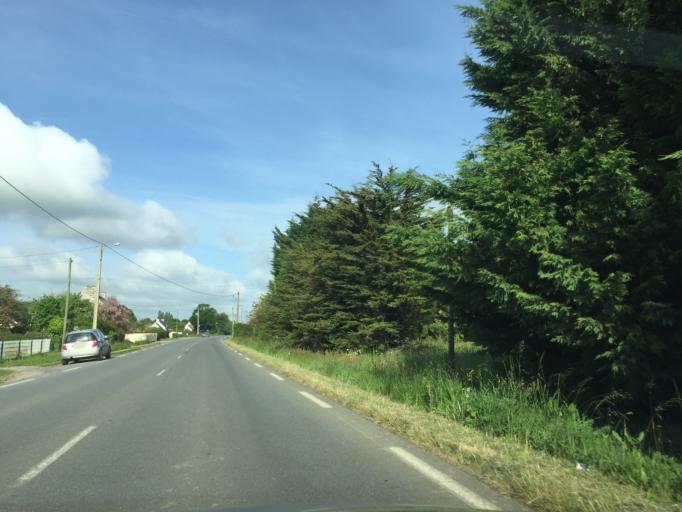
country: FR
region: Brittany
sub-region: Departement des Cotes-d'Armor
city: Matignon
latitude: 48.5938
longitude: -2.2551
